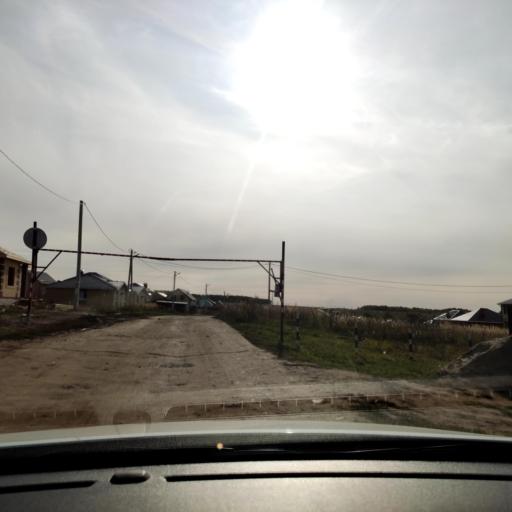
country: RU
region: Tatarstan
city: Vysokaya Gora
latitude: 55.8663
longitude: 49.3690
